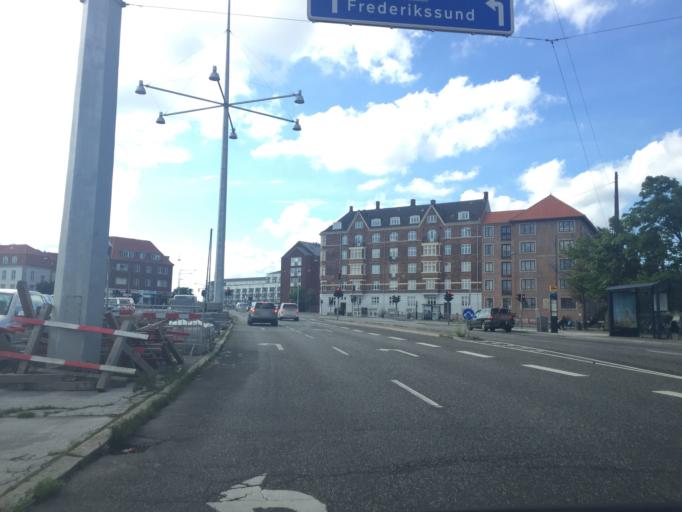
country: DK
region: Capital Region
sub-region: Frederiksberg Kommune
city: Frederiksberg
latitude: 55.7060
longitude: 12.5169
